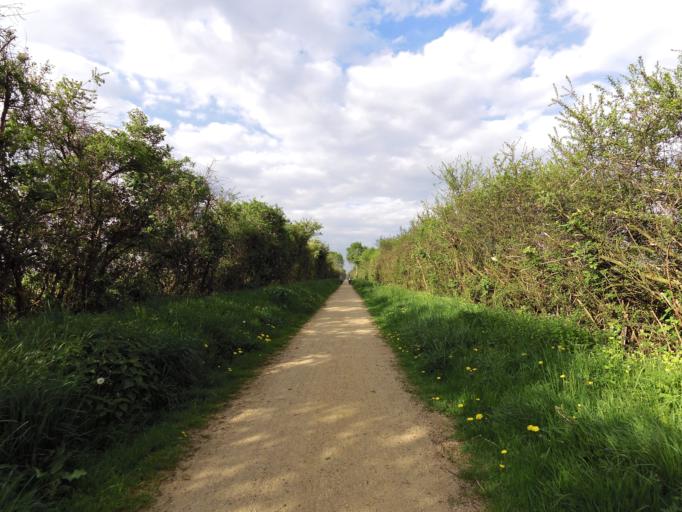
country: DE
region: North Rhine-Westphalia
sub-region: Regierungsbezirk Dusseldorf
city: Kleve
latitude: 51.8091
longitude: 6.1542
